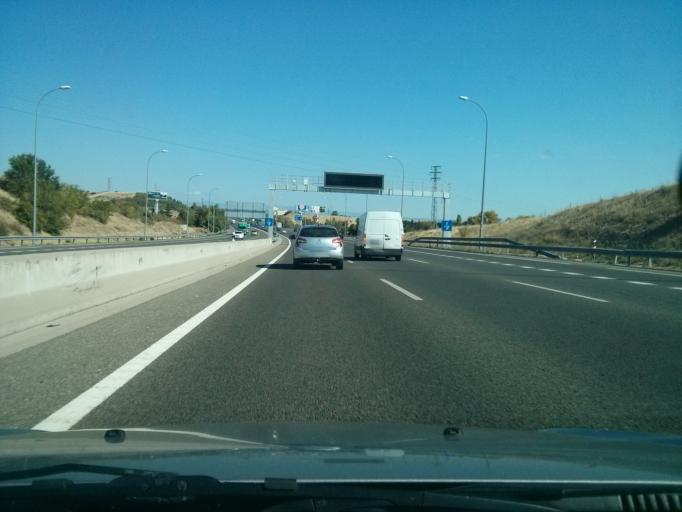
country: ES
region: Madrid
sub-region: Provincia de Madrid
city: San Sebastian de los Reyes
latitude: 40.5705
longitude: -3.5876
